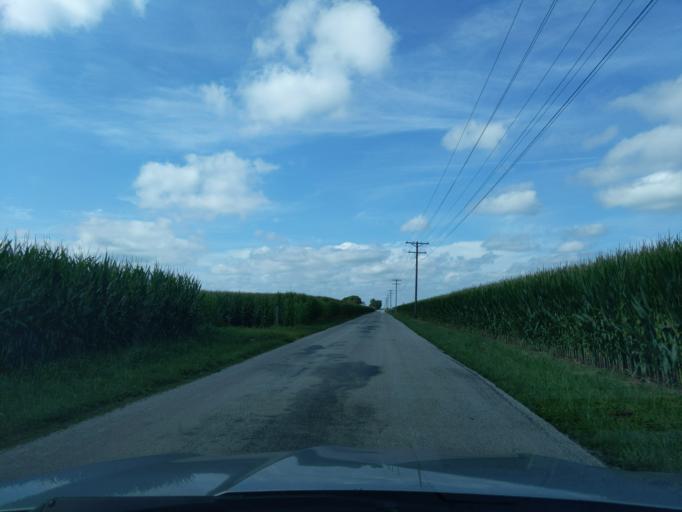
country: US
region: Indiana
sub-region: Ripley County
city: Batesville
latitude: 39.2750
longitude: -85.3476
